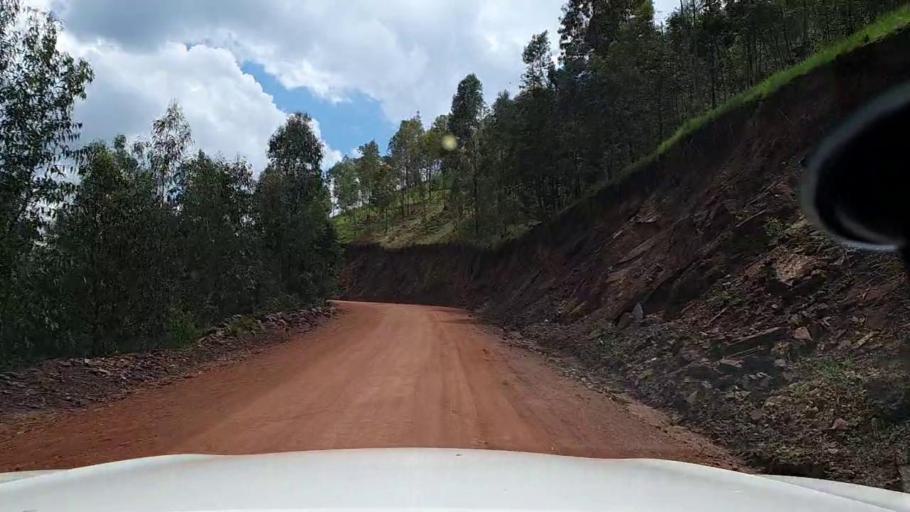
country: RW
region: Northern Province
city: Byumba
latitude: -1.7527
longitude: 29.8449
